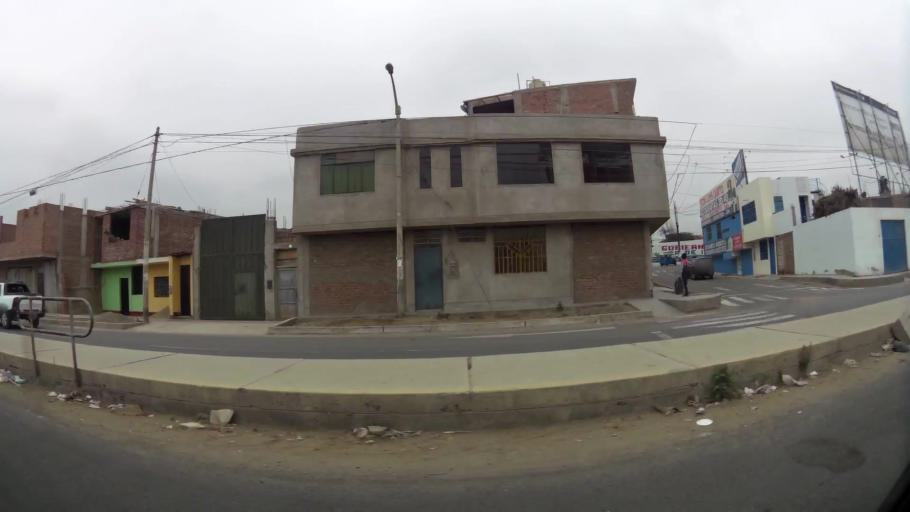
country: PE
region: La Libertad
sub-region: Provincia de Trujillo
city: La Esperanza
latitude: -8.0847
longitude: -79.0444
